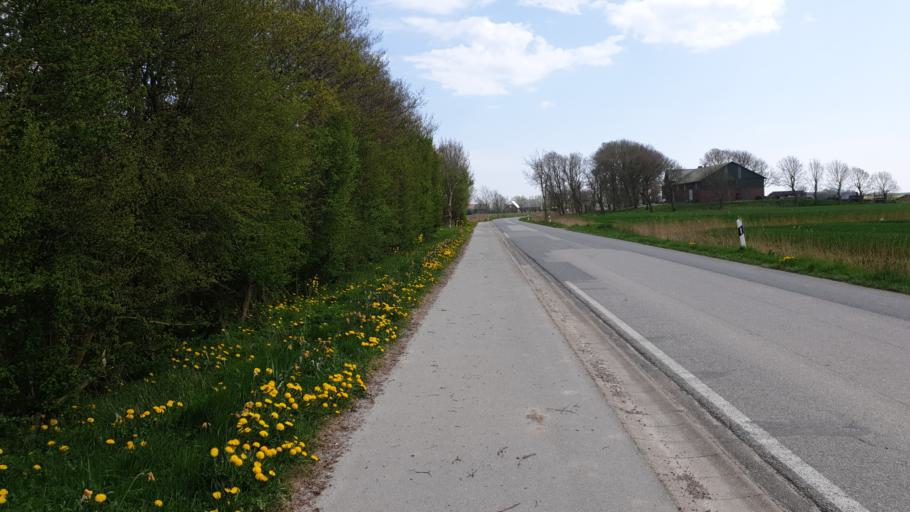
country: DE
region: Schleswig-Holstein
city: Elisabeth-Sophien-Koog
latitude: 54.4739
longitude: 8.8793
